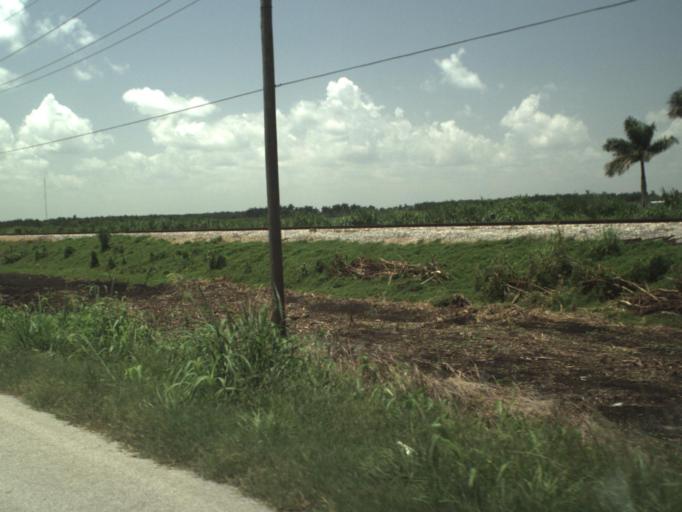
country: US
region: Florida
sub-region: Palm Beach County
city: Pahokee
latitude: 26.8259
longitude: -80.6461
